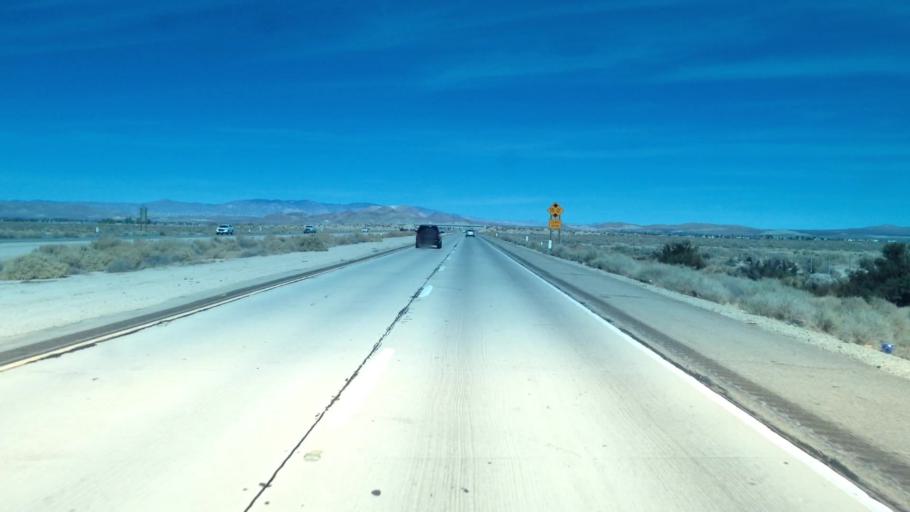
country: US
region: California
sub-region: Kern County
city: Rosamond
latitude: 34.7976
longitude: -118.1706
